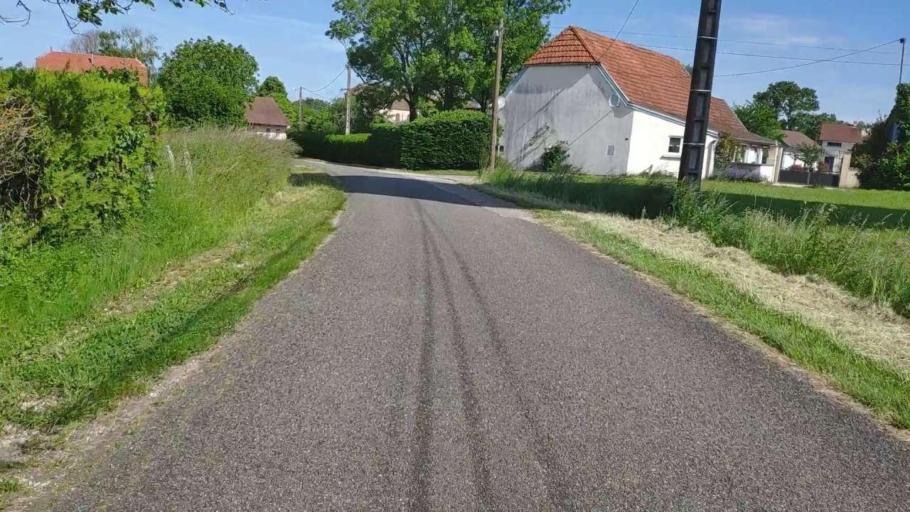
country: FR
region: Franche-Comte
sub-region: Departement du Jura
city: Bletterans
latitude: 46.7100
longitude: 5.4549
